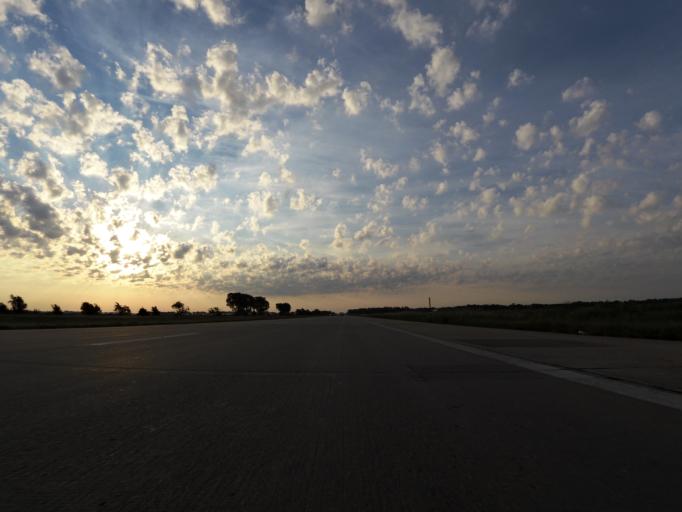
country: US
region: Kansas
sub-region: Reno County
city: Haven
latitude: 37.8882
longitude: -97.7445
